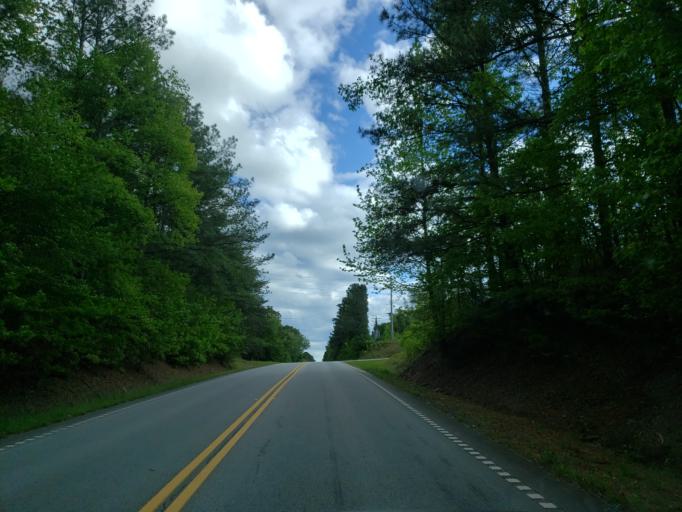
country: US
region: Georgia
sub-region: Haralson County
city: Tallapoosa
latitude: 33.8522
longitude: -85.2914
